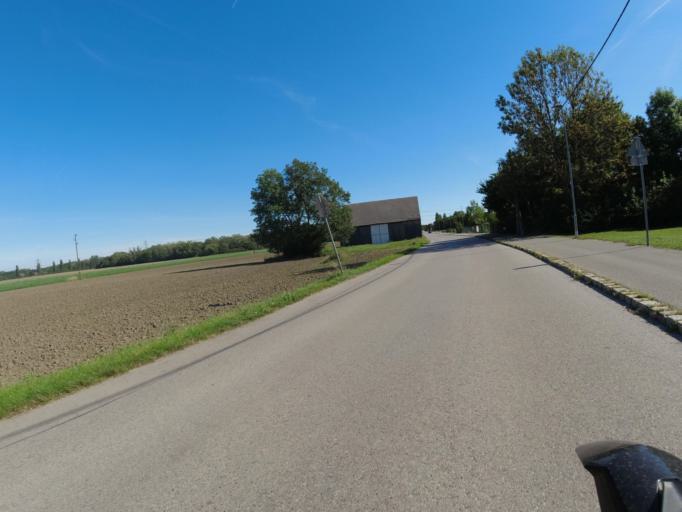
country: AT
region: Lower Austria
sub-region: Politischer Bezirk Baden
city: Traiskirchen
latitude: 48.0230
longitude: 16.3095
